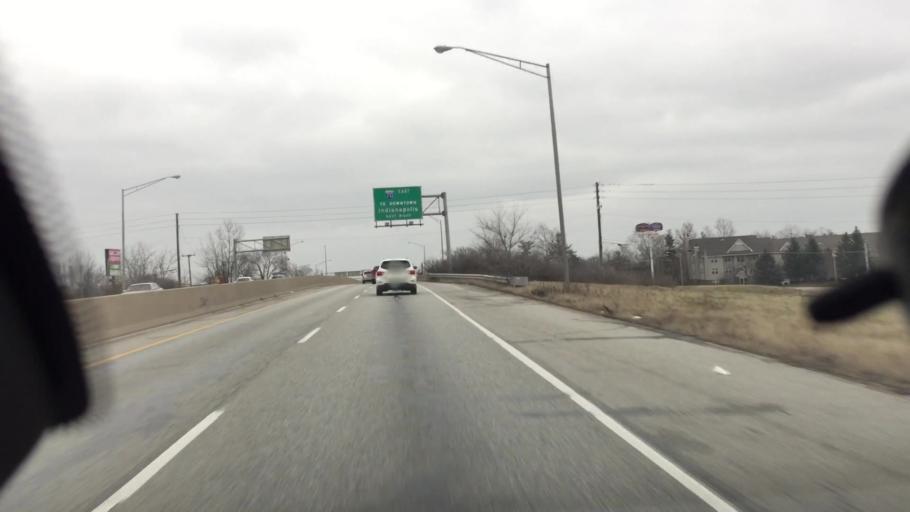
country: US
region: Indiana
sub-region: Marion County
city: Speedway
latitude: 39.7304
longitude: -86.2516
